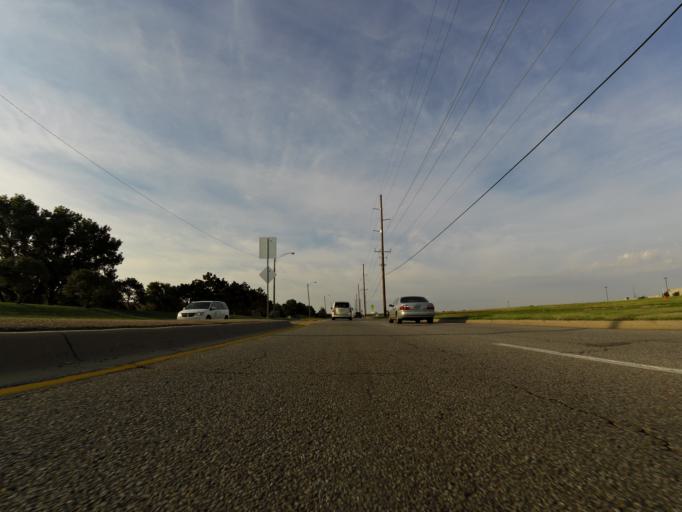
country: US
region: Kansas
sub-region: Sedgwick County
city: Bellaire
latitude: 37.7365
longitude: -97.2624
